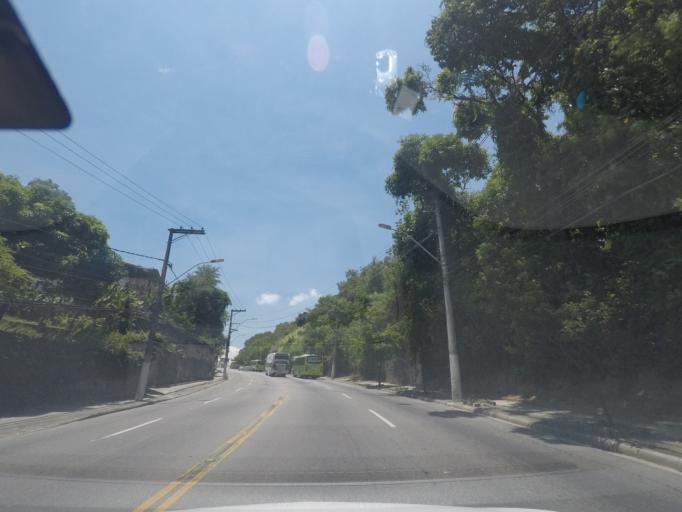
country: BR
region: Rio de Janeiro
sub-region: Niteroi
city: Niteroi
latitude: -22.9104
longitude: -43.0704
